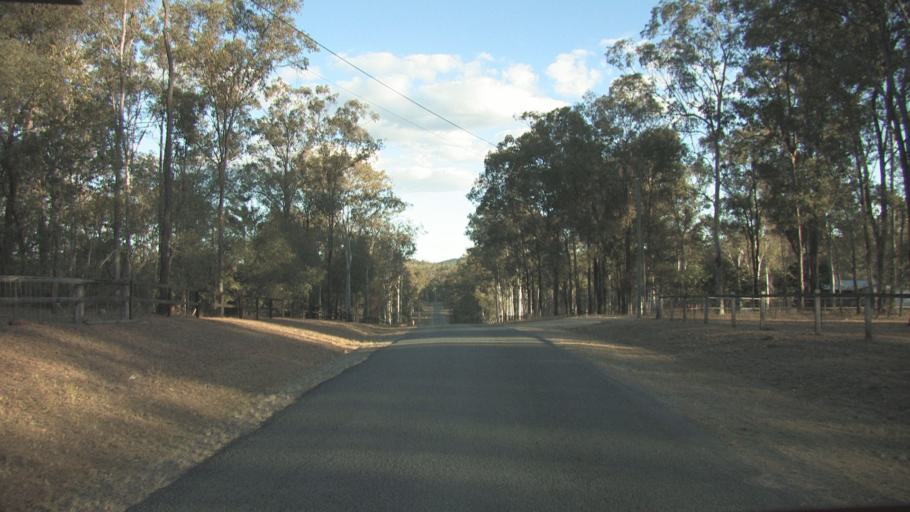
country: AU
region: Queensland
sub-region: Logan
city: Cedar Vale
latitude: -27.8514
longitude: 153.0895
